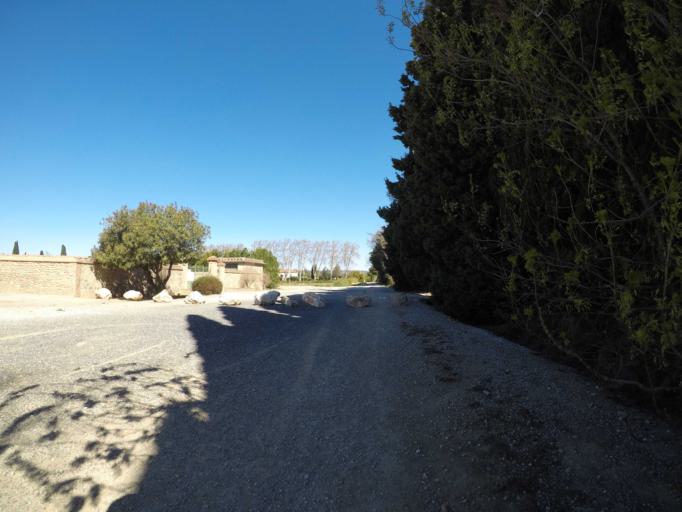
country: FR
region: Languedoc-Roussillon
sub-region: Departement des Pyrenees-Orientales
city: Corneilla-la-Riviere
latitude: 42.6834
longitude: 2.7262
